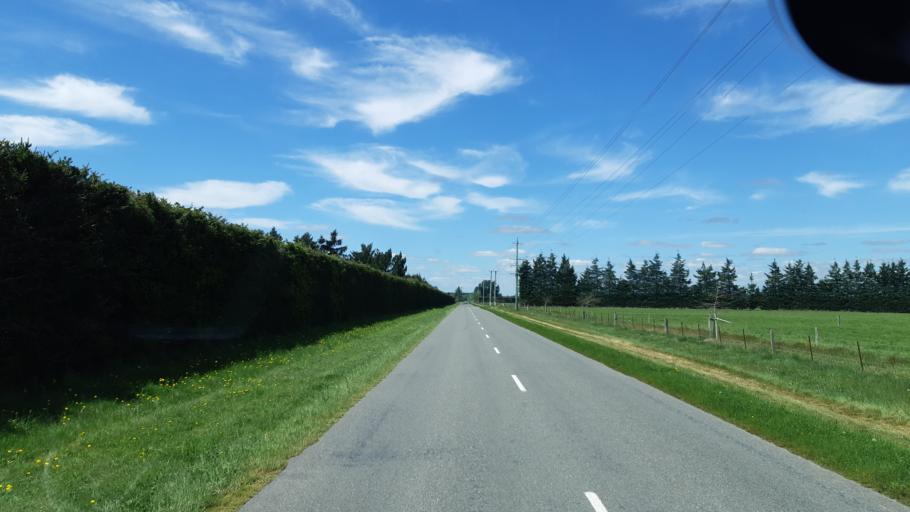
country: NZ
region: Canterbury
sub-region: Ashburton District
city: Methven
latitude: -43.7278
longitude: 171.5031
